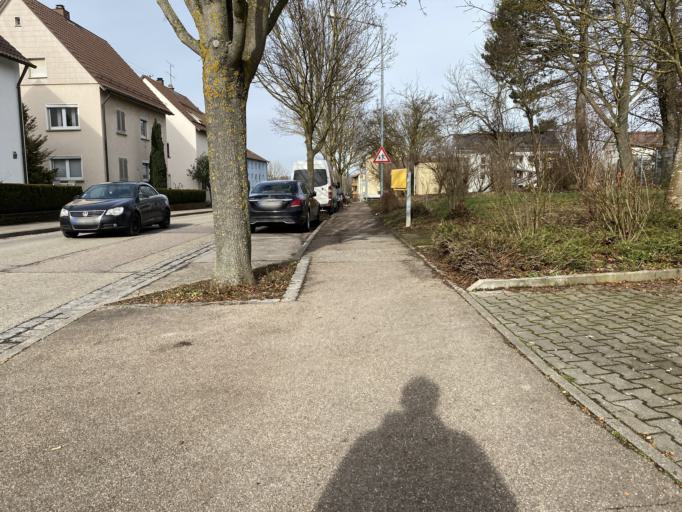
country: DE
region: Baden-Wuerttemberg
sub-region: Regierungsbezirk Stuttgart
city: Vaihingen an der Enz
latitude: 48.9388
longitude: 8.9568
